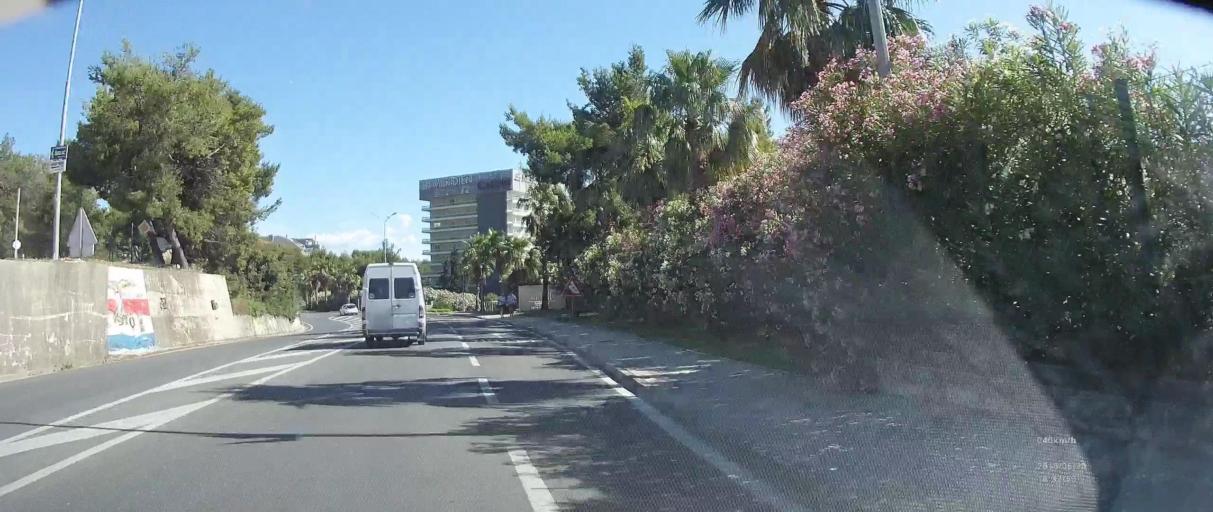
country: HR
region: Splitsko-Dalmatinska
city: Podstrana
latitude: 43.4945
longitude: 16.5387
